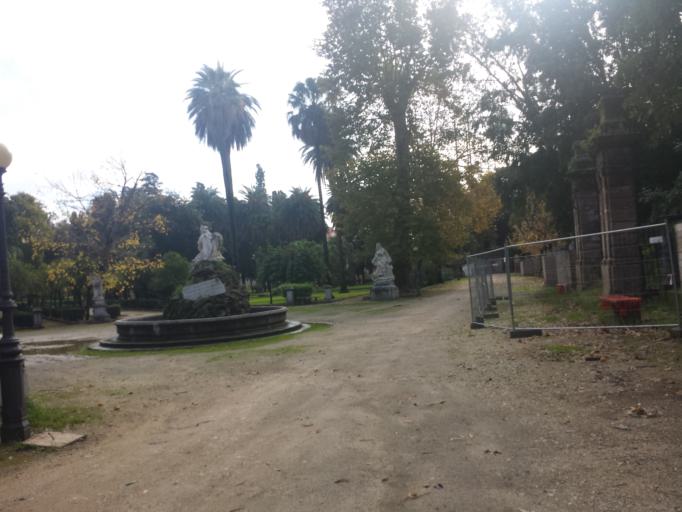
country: IT
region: Sicily
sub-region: Palermo
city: Palermo
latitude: 38.1131
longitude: 13.3743
